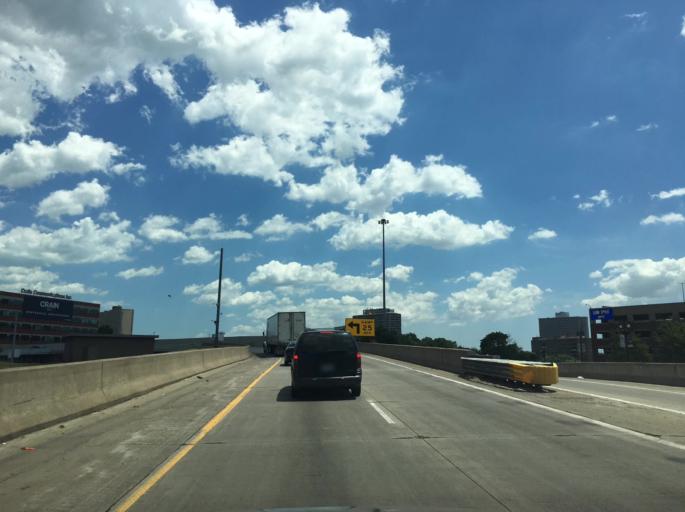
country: US
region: Michigan
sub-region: Wayne County
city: Detroit
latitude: 42.3419
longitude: -83.0452
